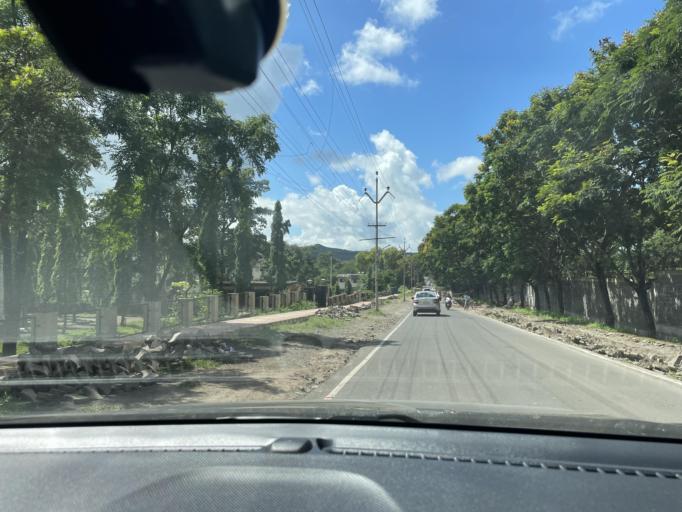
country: IN
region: Maharashtra
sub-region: Pune Division
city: Shivaji Nagar
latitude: 18.5260
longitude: 73.7810
